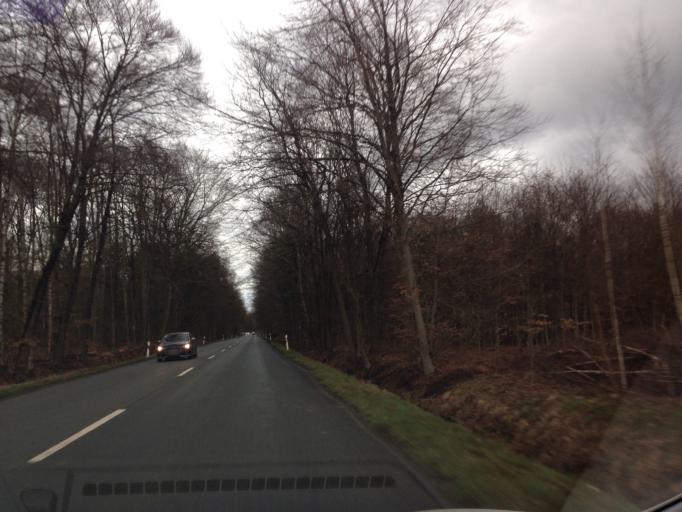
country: DE
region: North Rhine-Westphalia
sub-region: Regierungsbezirk Munster
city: Senden
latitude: 51.8387
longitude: 7.5427
